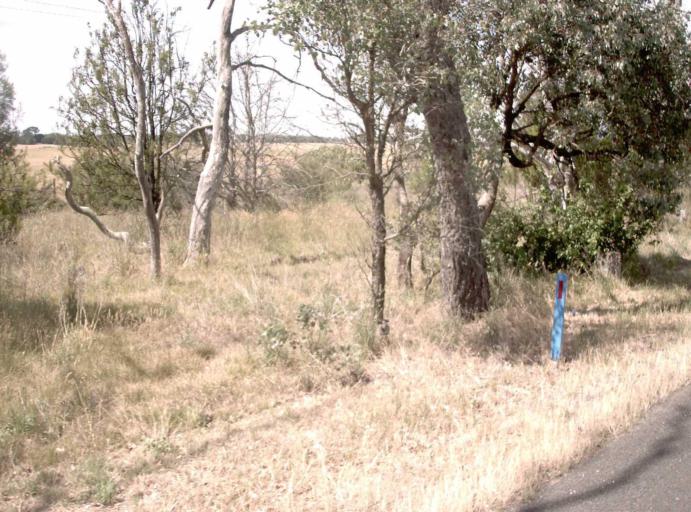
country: AU
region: Victoria
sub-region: Wellington
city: Sale
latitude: -37.9348
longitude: 147.1721
